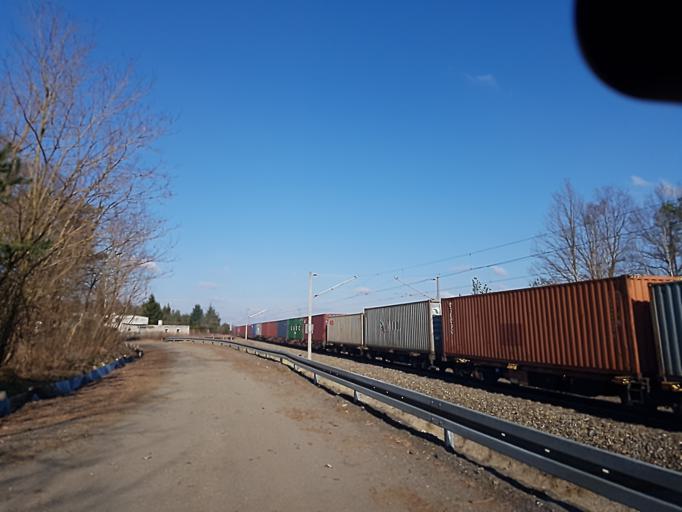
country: DE
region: Brandenburg
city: Doberlug-Kirchhain
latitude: 51.6052
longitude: 13.5647
